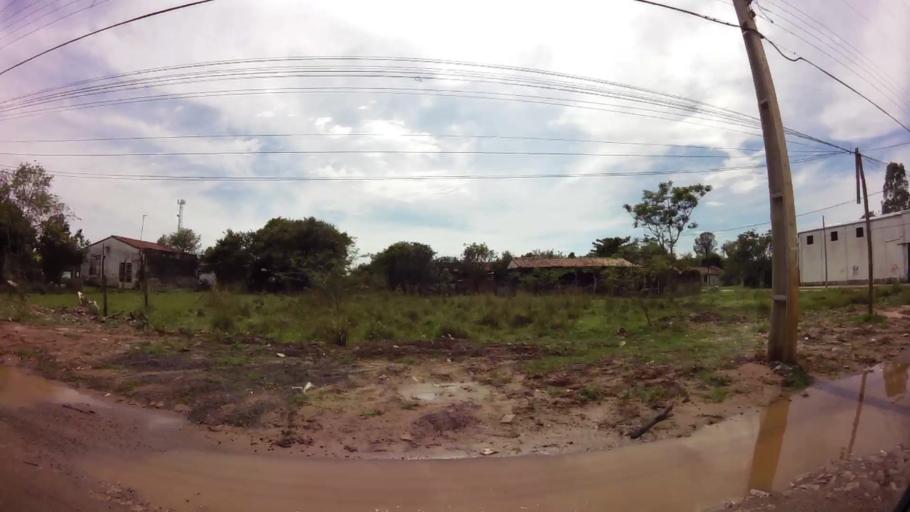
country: PY
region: Central
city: Limpio
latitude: -25.1779
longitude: -57.4804
